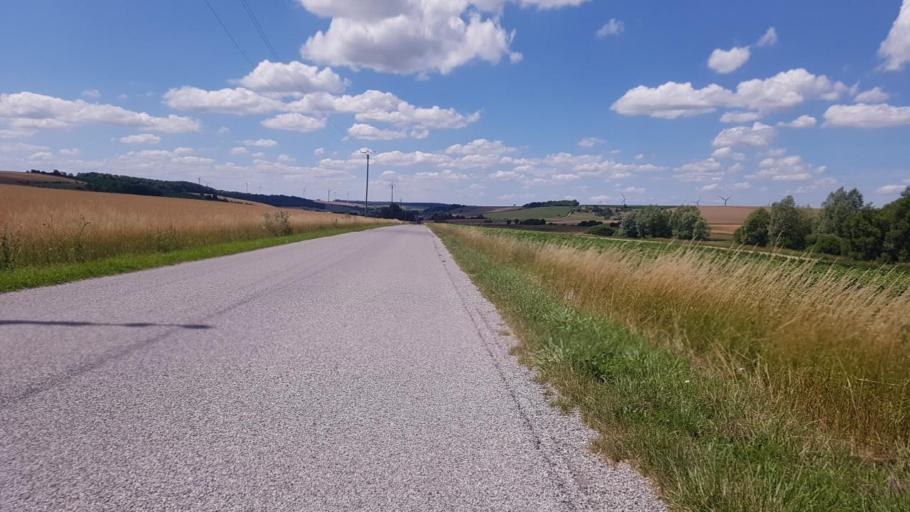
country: FR
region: Lorraine
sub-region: Departement de la Meuse
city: Vacon
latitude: 48.6530
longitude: 5.5307
